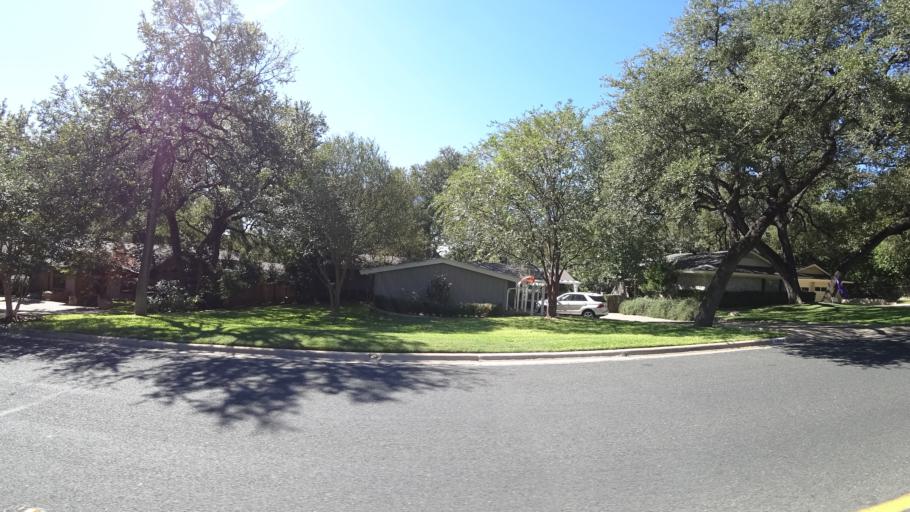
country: US
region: Texas
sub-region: Travis County
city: West Lake Hills
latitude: 30.3204
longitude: -97.7685
